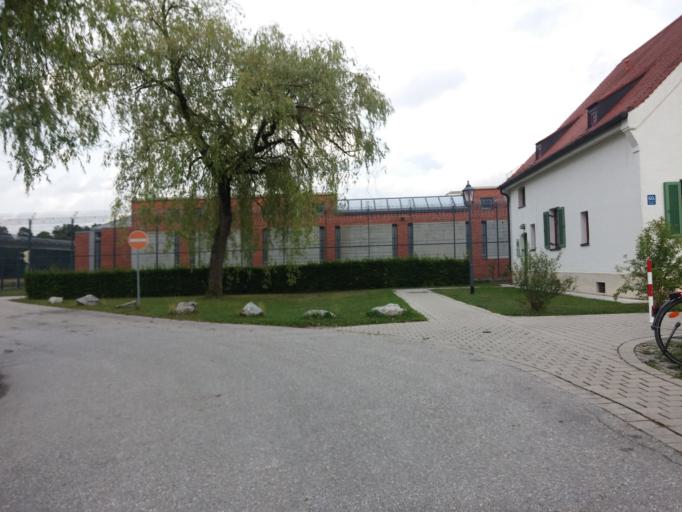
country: DE
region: Bavaria
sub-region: Upper Bavaria
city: Vaterstetten
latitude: 48.1182
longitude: 11.7514
